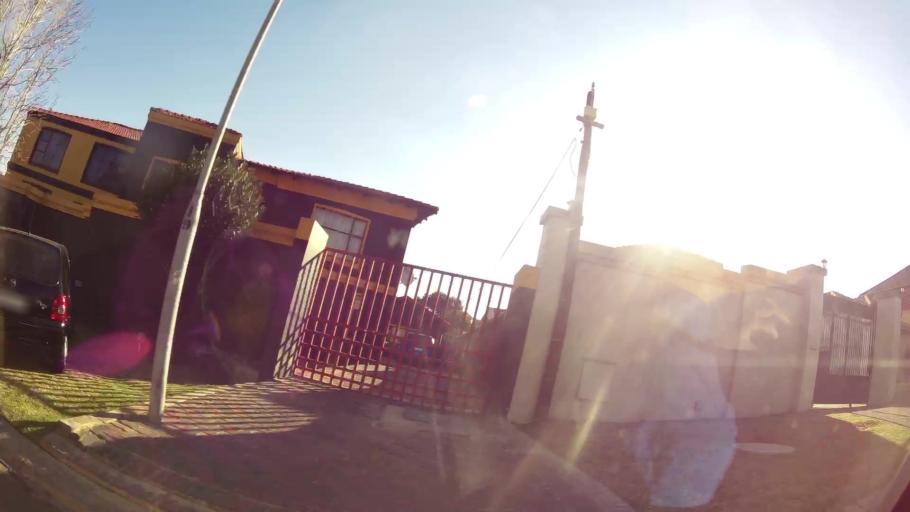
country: ZA
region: Gauteng
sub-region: City of Johannesburg Metropolitan Municipality
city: Johannesburg
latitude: -26.2956
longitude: 28.0605
